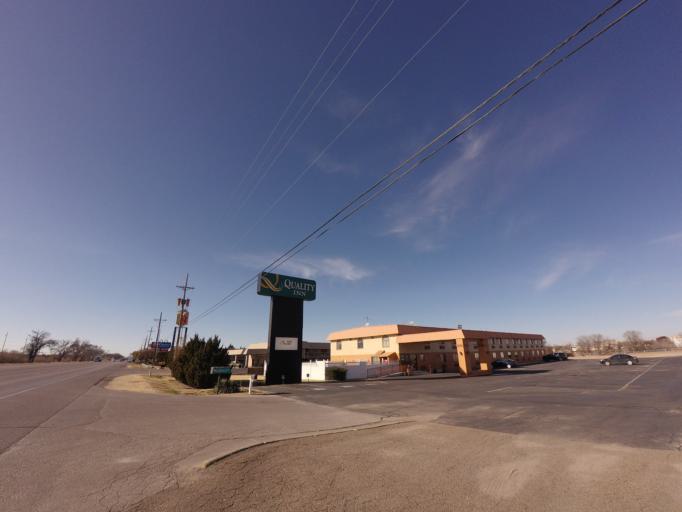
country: US
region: New Mexico
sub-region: Curry County
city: Clovis
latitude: 34.3956
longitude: -103.1662
